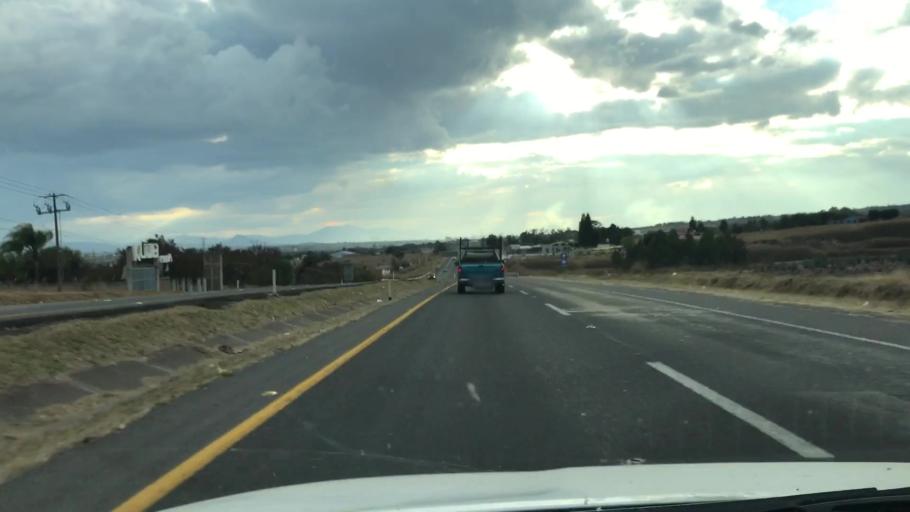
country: MX
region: Guanajuato
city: Penjamo
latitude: 20.4151
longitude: -101.7302
